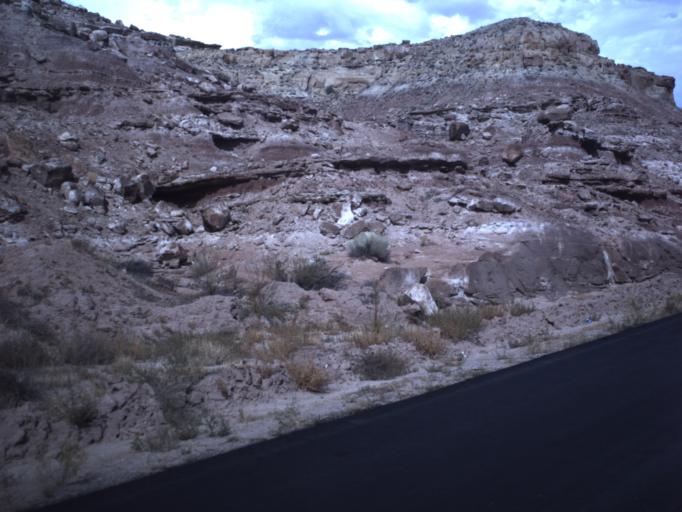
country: US
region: Utah
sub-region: San Juan County
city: Blanding
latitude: 37.2576
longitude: -109.2802
